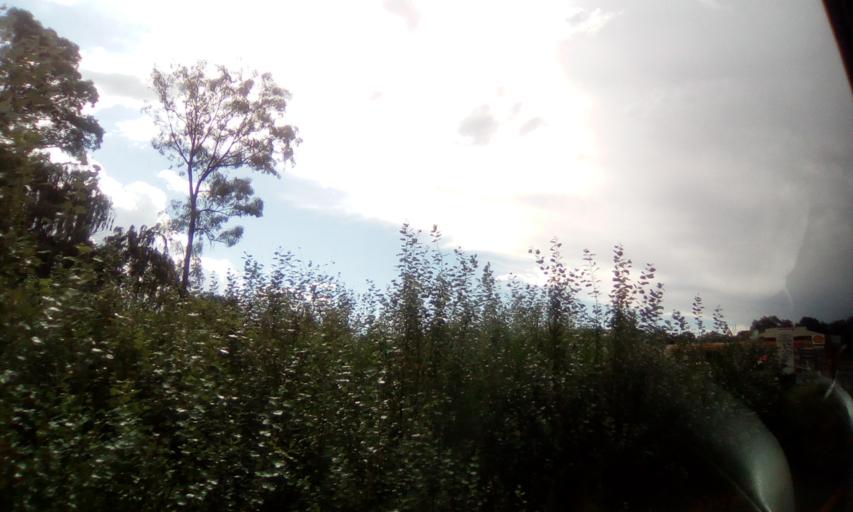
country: ZA
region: Orange Free State
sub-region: Thabo Mofutsanyana District Municipality
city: Ladybrand
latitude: -29.1991
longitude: 27.4634
